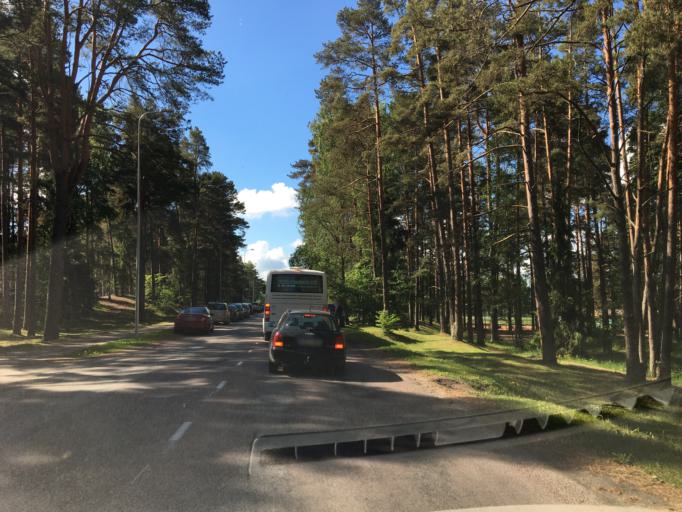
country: EE
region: Tartu
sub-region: Elva linn
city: Elva
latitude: 58.2268
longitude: 26.4071
